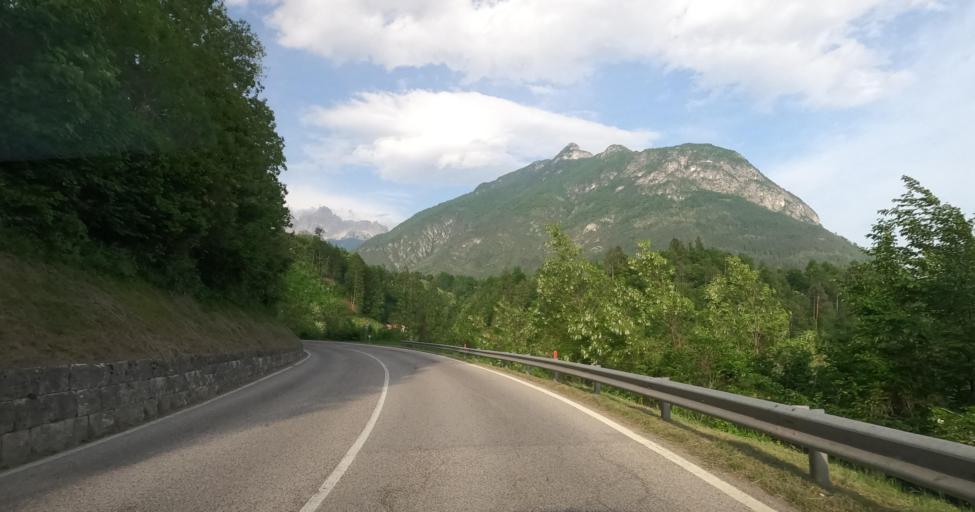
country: IT
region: Veneto
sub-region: Provincia di Belluno
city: Agordo
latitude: 46.2698
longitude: 12.0372
